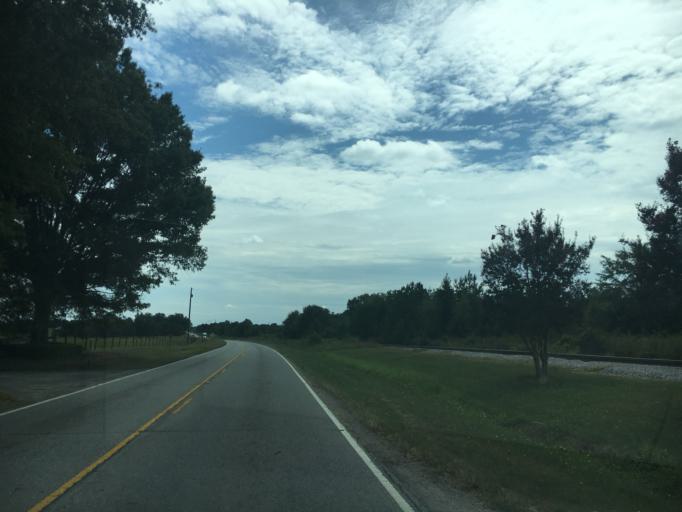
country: US
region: South Carolina
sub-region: Greenville County
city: Fountain Inn
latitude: 34.6283
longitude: -82.1312
